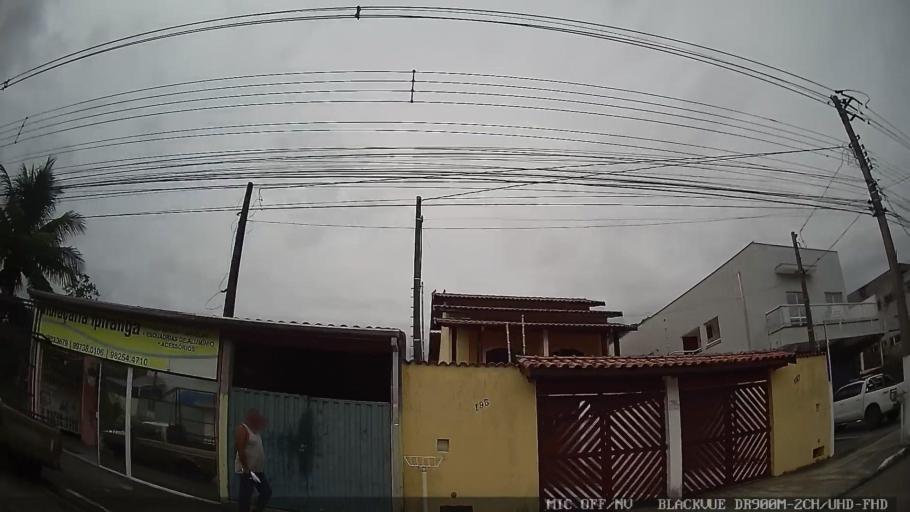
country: BR
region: Sao Paulo
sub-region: Caraguatatuba
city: Caraguatatuba
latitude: -23.6199
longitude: -45.3962
